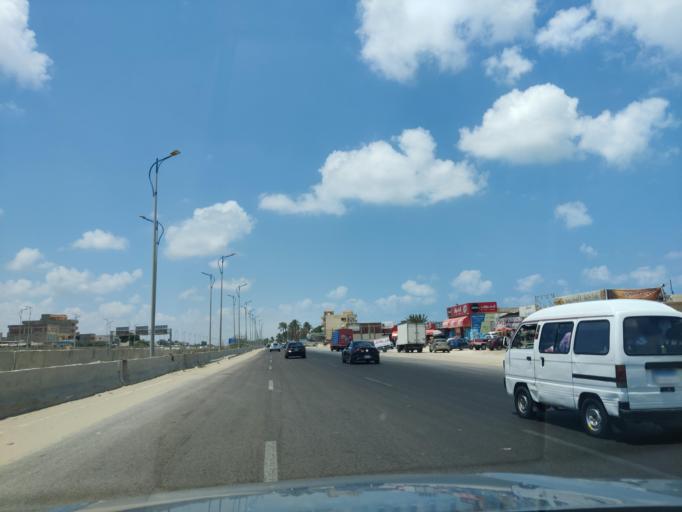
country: EG
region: Alexandria
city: Alexandria
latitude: 31.0110
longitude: 29.6270
